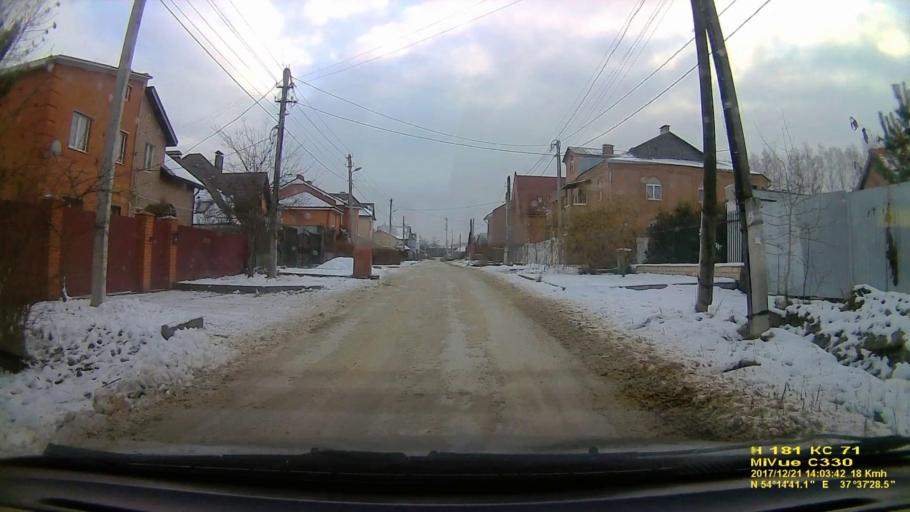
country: RU
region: Tula
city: Gorelki
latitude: 54.2447
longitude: 37.6246
